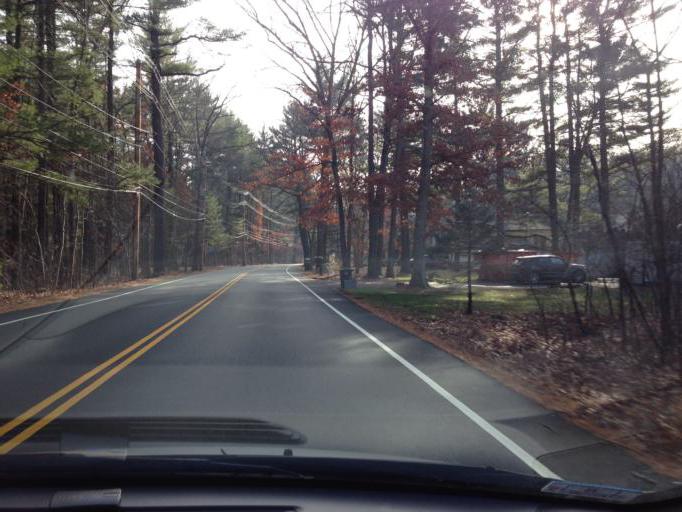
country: US
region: Massachusetts
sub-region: Middlesex County
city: Bedford
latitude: 42.5056
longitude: -71.3030
